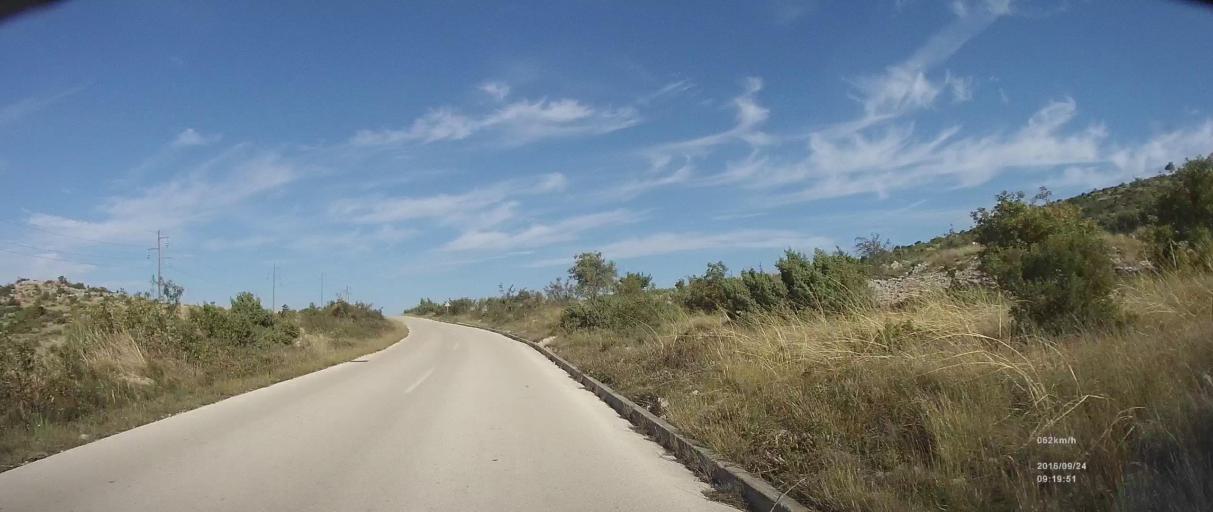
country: HR
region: Zadarska
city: Polaca
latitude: 44.0647
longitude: 15.5011
